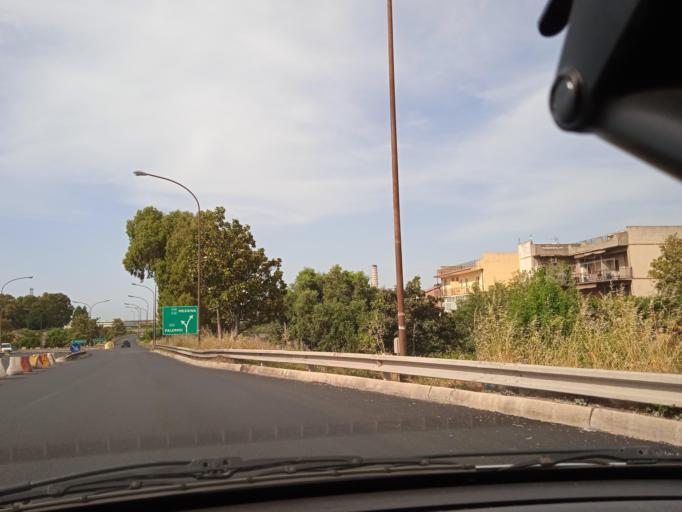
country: IT
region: Sicily
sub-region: Messina
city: San Filippo del Mela
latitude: 38.1897
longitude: 15.2745
